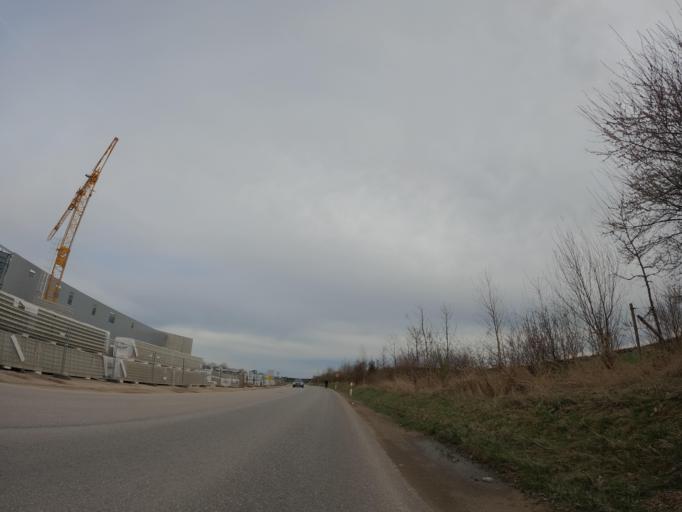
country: DE
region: Bavaria
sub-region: Upper Bavaria
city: Oberhaching
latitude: 48.0299
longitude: 11.6121
